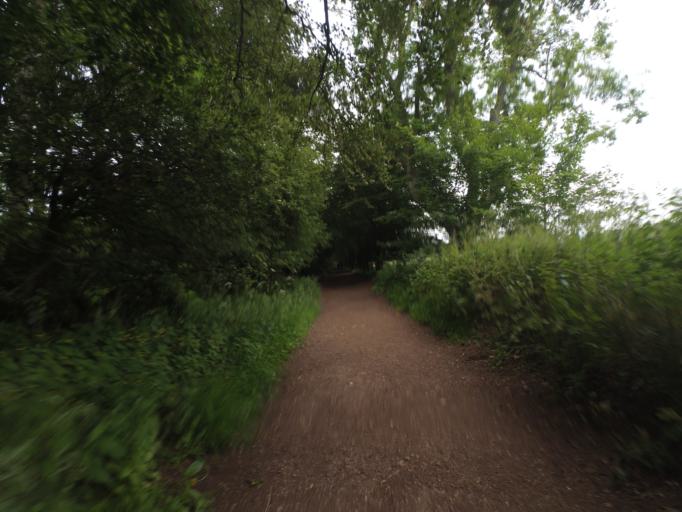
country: GB
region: Scotland
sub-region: East Lothian
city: East Linton
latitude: 56.0197
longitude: -2.5984
